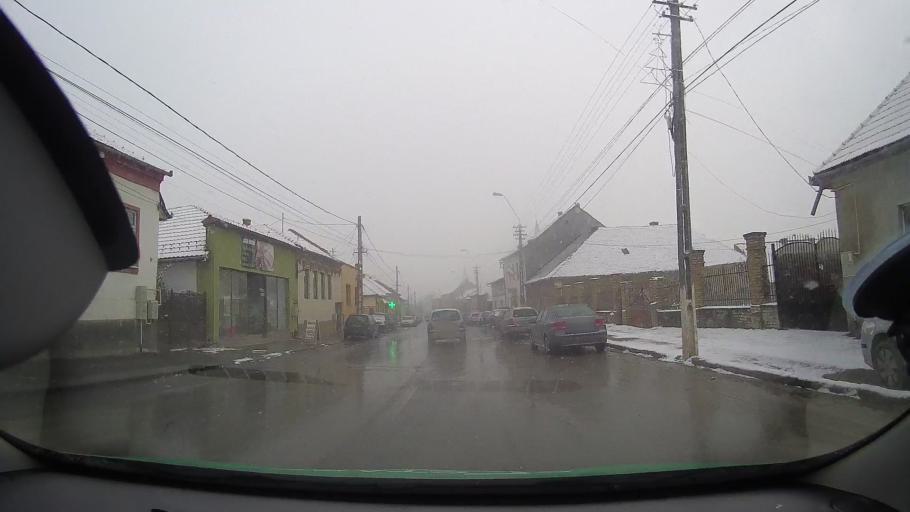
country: RO
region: Alba
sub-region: Municipiul Aiud
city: Aiud
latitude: 46.3103
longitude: 23.7137
